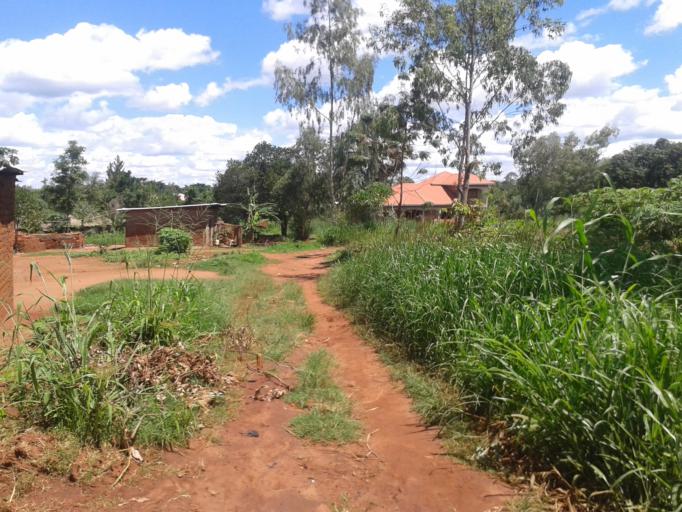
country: UG
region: Northern Region
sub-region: Gulu District
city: Gulu
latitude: 2.7688
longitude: 32.3193
